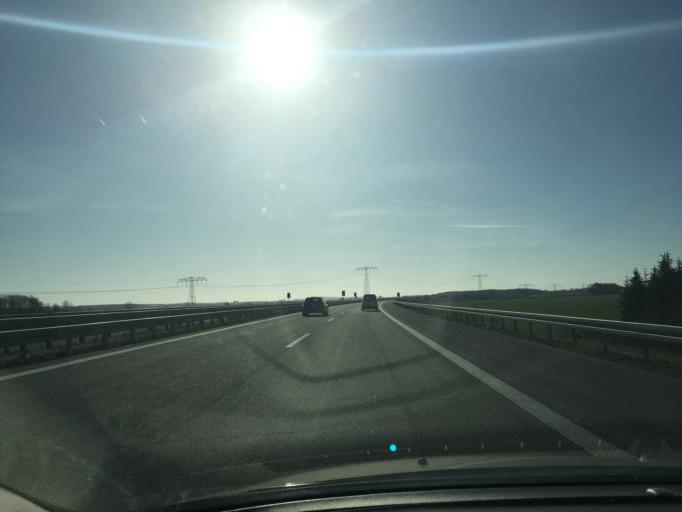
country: DE
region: Saxony
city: Frohburg
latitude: 51.0747
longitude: 12.6009
